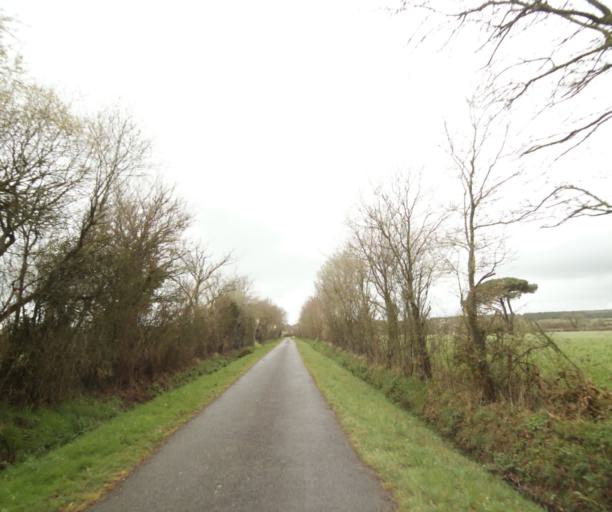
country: FR
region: Pays de la Loire
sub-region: Departement de la Loire-Atlantique
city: Quilly
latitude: 47.4578
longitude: -1.9009
